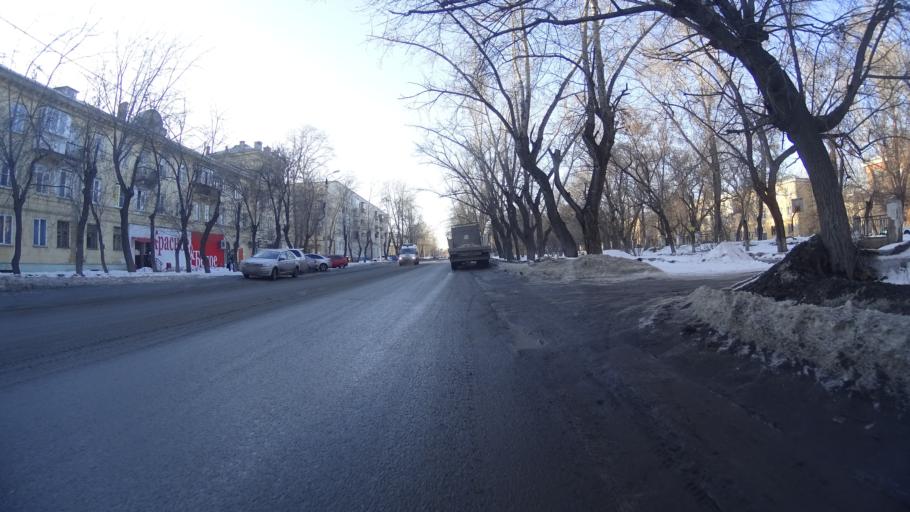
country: RU
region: Chelyabinsk
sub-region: Gorod Chelyabinsk
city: Chelyabinsk
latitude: 55.1283
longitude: 61.4686
